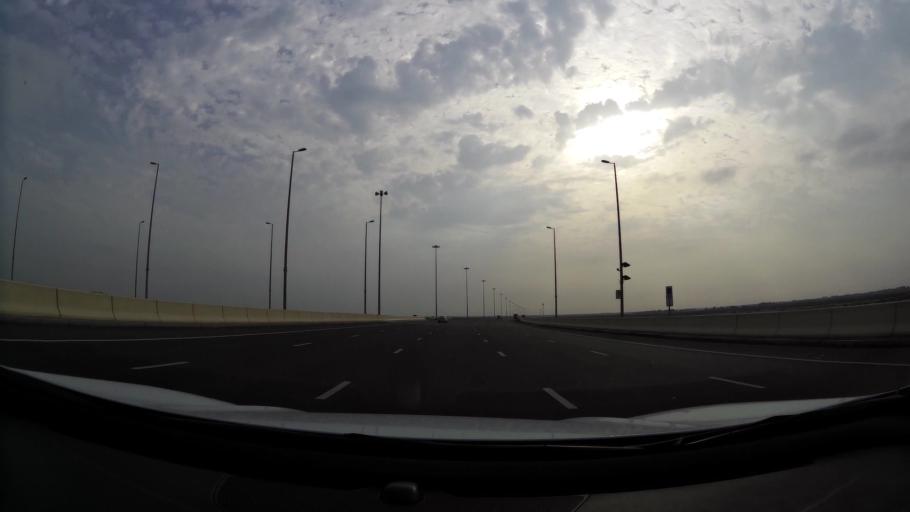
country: AE
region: Abu Dhabi
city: Abu Dhabi
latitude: 24.5491
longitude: 54.4580
